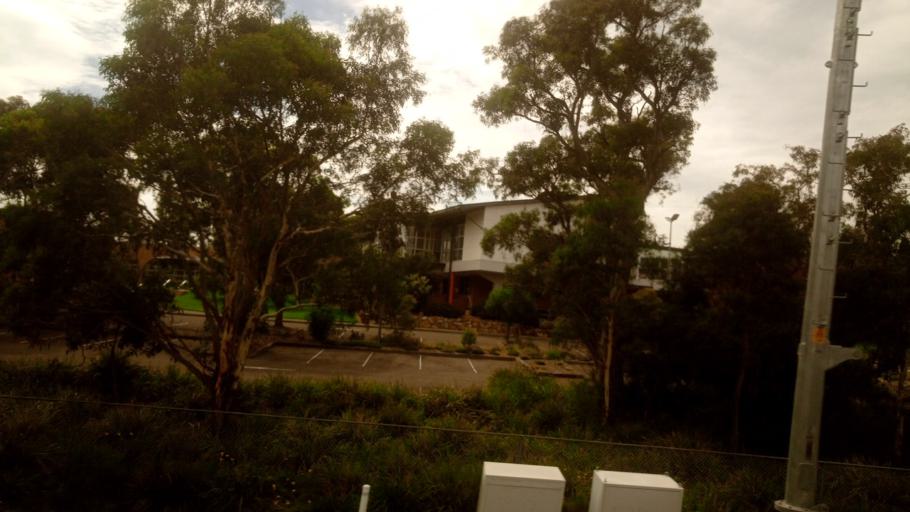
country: AU
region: New South Wales
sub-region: Blue Mountains Municipality
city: Leura
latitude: -33.7079
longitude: 150.3667
